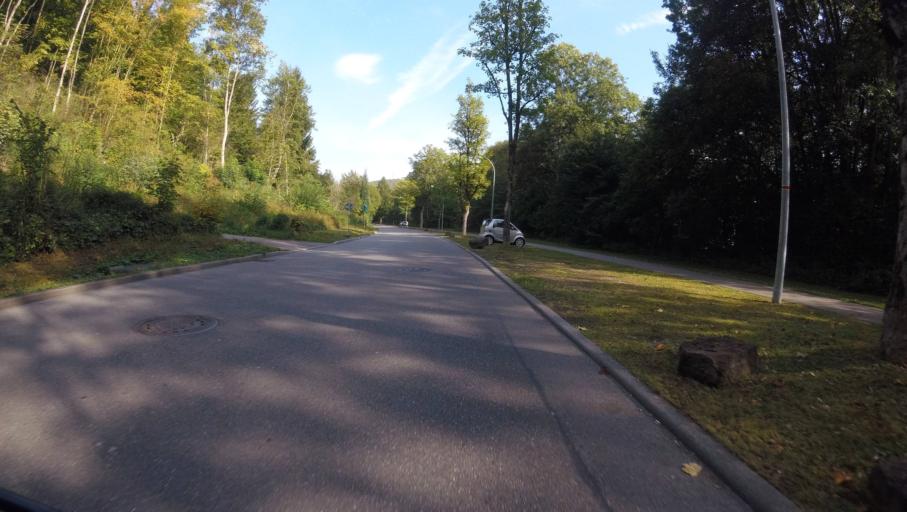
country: DE
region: Baden-Wuerttemberg
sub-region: Karlsruhe Region
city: Nagold
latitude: 48.5419
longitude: 8.7272
